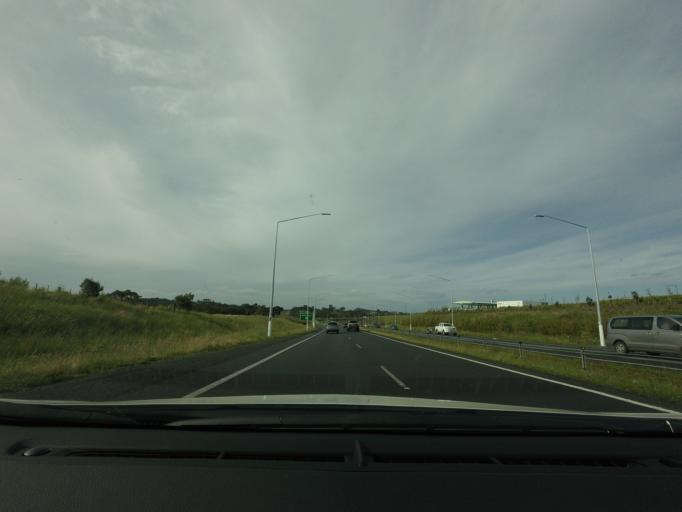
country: NZ
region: Auckland
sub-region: Auckland
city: Rothesay Bay
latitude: -36.6070
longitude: 174.6606
